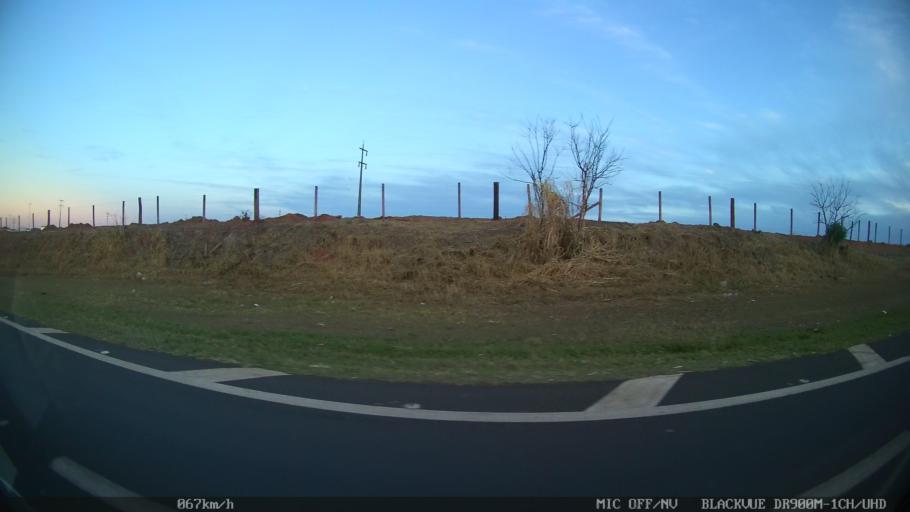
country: BR
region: Sao Paulo
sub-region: Catanduva
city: Catanduva
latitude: -21.1302
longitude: -49.0120
